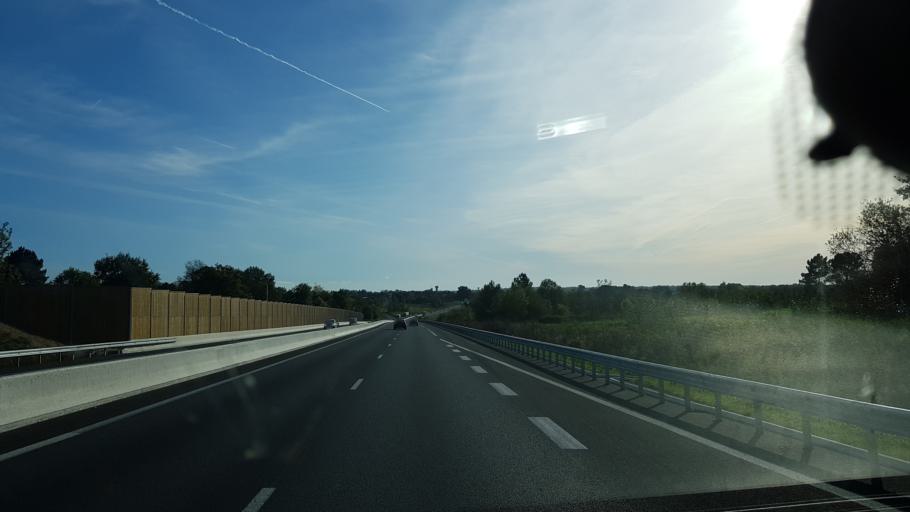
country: FR
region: Poitou-Charentes
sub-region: Departement de la Charente-Maritime
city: Chevanceaux
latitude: 45.3217
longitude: -0.2290
